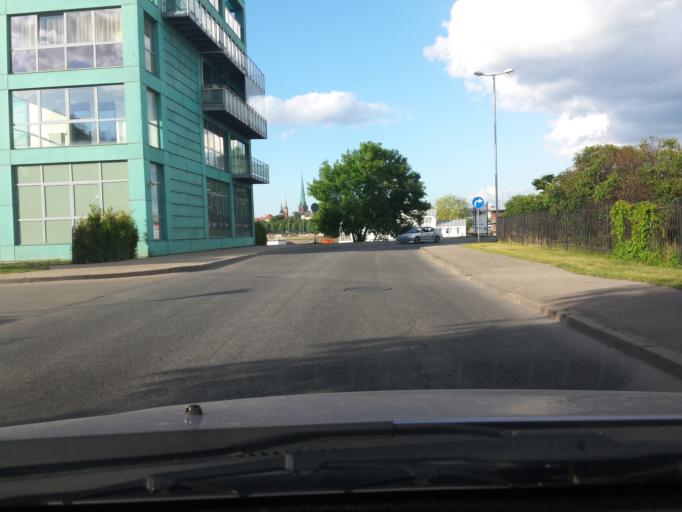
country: LV
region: Riga
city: Riga
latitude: 56.9448
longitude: 24.0927
